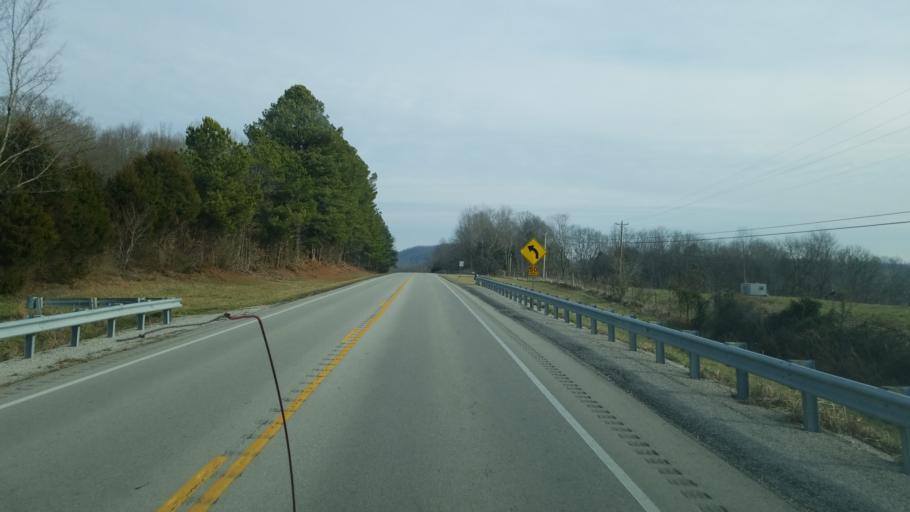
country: US
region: Kentucky
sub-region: Casey County
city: Liberty
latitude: 37.3516
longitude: -84.8726
